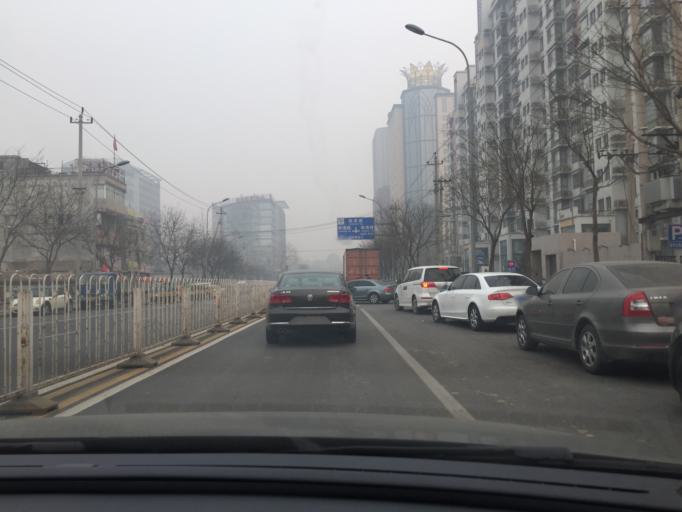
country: CN
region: Beijing
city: Qinghe
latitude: 40.0138
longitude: 116.3436
